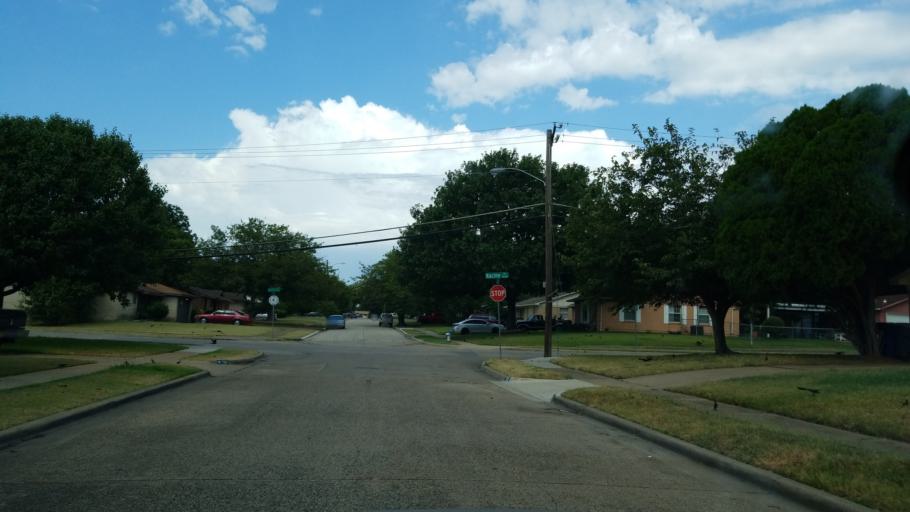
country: US
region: Texas
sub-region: Dallas County
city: DeSoto
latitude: 32.6547
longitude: -96.8351
